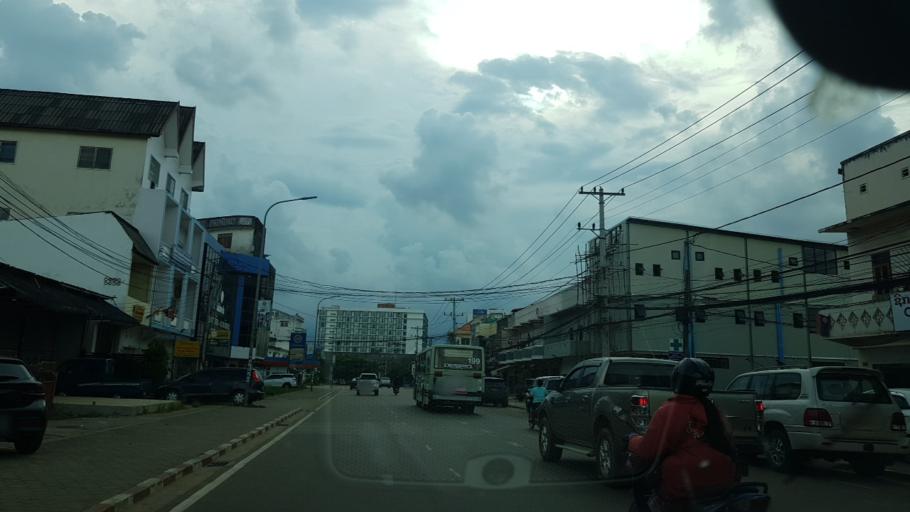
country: LA
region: Vientiane
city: Vientiane
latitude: 17.9694
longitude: 102.6008
